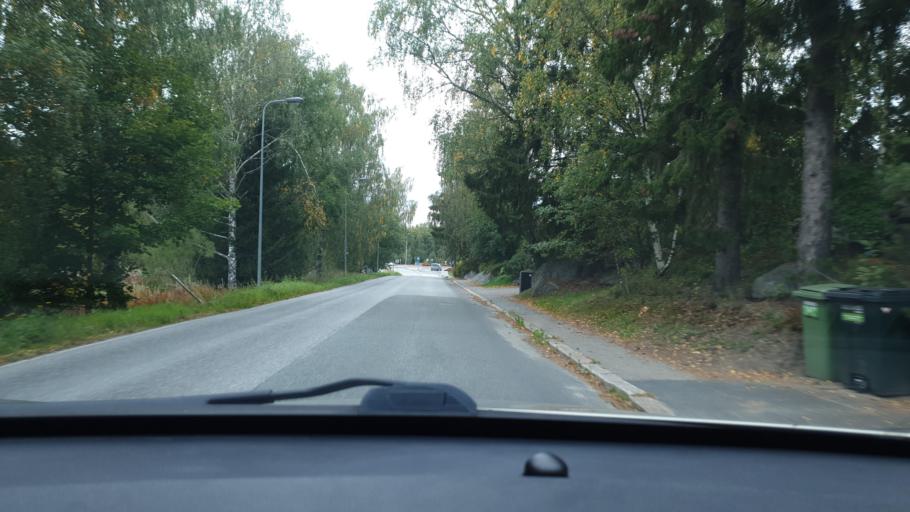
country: FI
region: Ostrobothnia
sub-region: Vaasa
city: Korsholm
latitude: 63.0972
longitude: 21.6617
